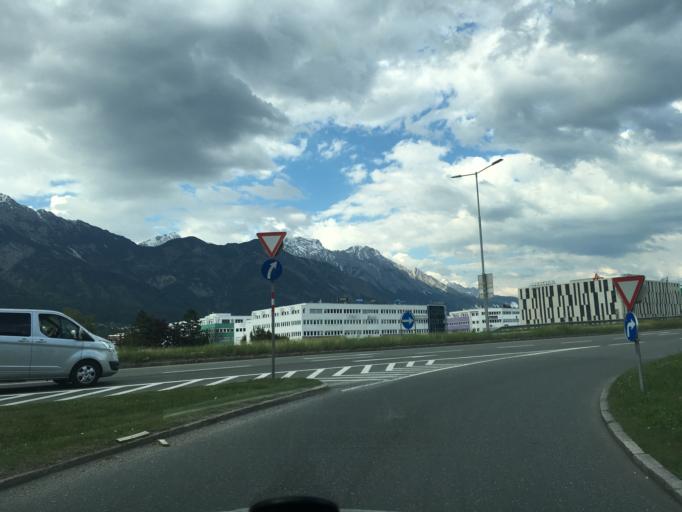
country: AT
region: Tyrol
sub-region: Politischer Bezirk Innsbruck Land
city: Ampass
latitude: 47.2635
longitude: 11.4326
